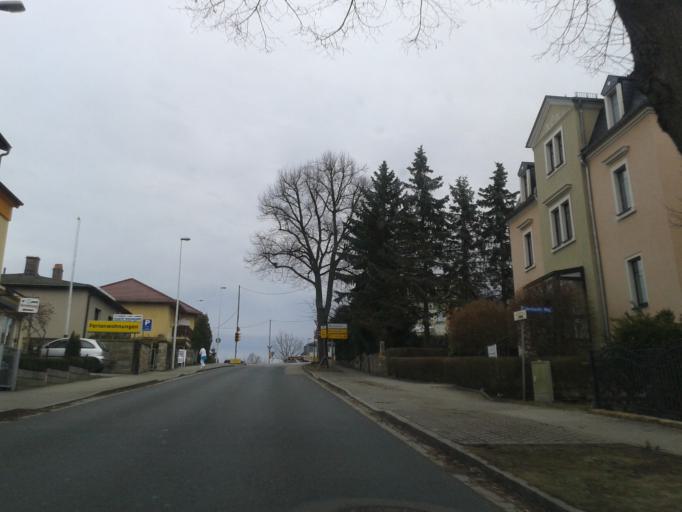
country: DE
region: Saxony
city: Bannewitz
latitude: 51.0029
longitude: 13.6840
